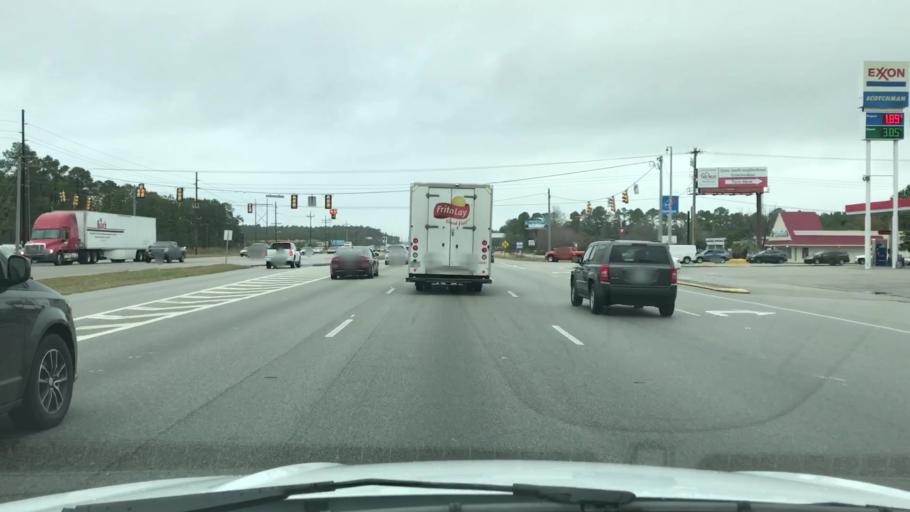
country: US
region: South Carolina
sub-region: Horry County
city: Forestbrook
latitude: 33.7749
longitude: -78.9824
